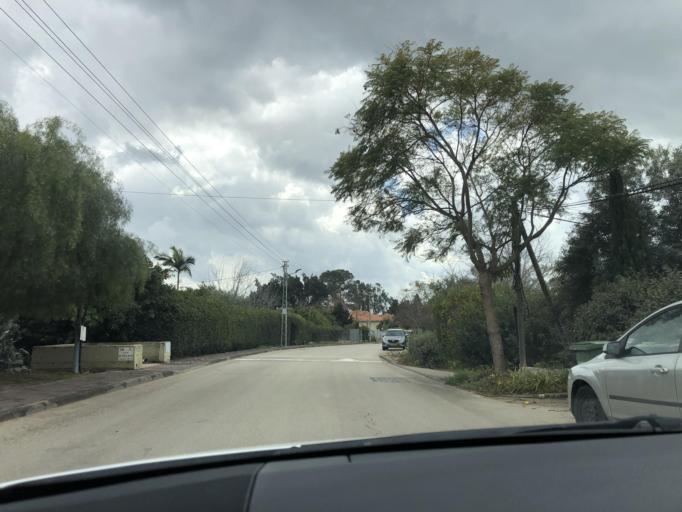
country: IL
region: Central District
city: Tel Mond
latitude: 32.2673
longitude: 34.9347
